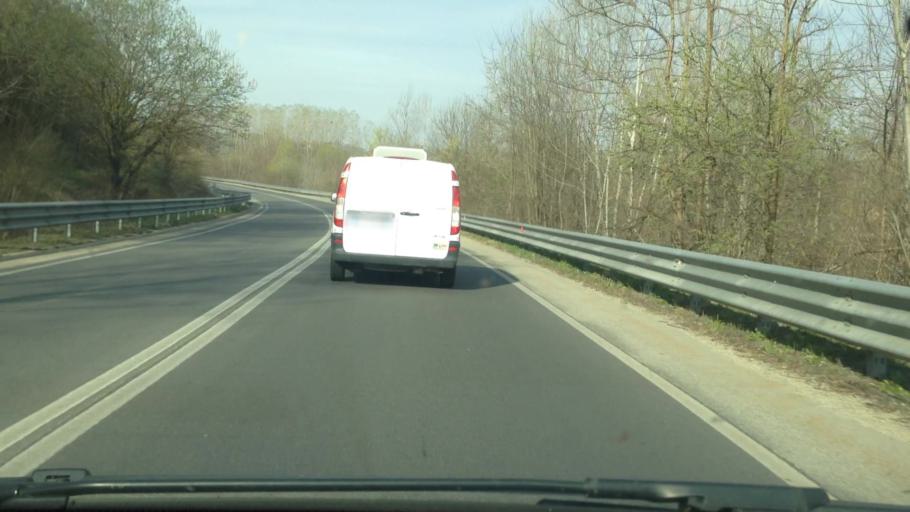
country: IT
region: Piedmont
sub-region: Provincia di Cuneo
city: Monta
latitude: 44.8053
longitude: 7.9710
